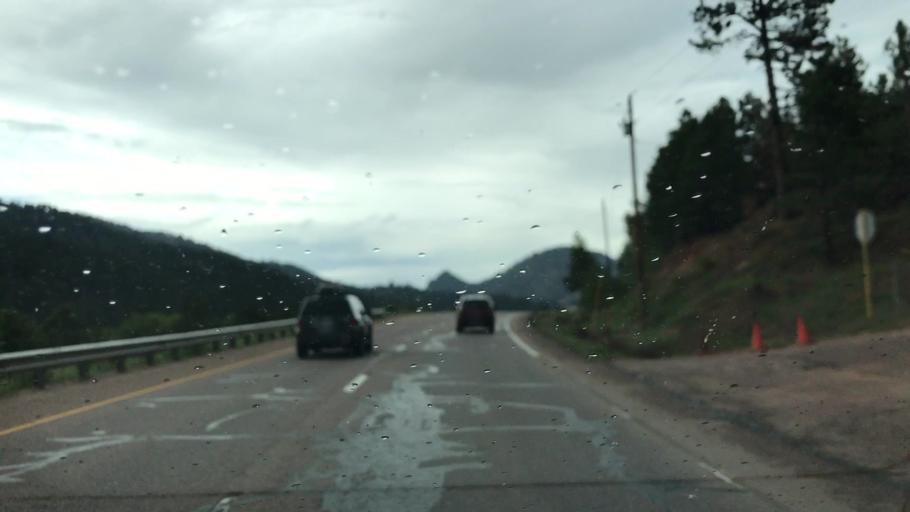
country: US
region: Colorado
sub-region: El Paso County
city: Cascade-Chipita Park
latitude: 38.9439
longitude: -105.0189
